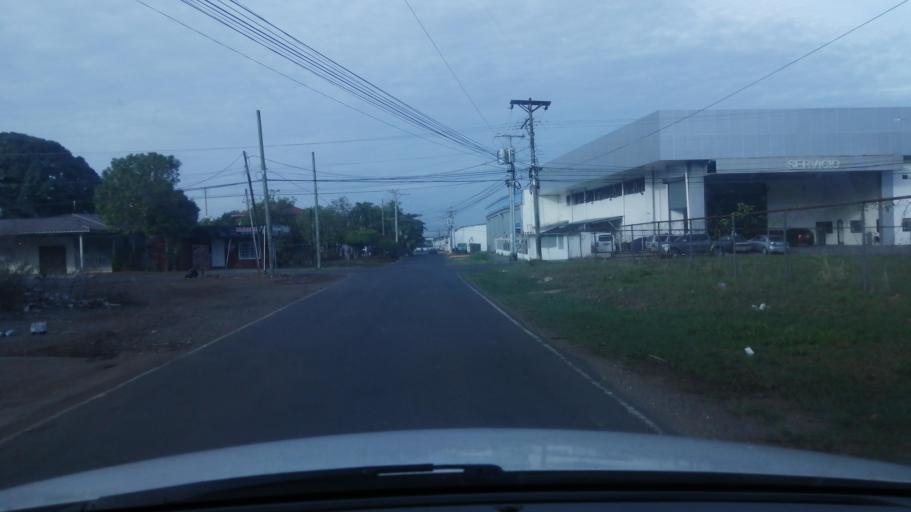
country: PA
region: Chiriqui
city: David
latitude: 8.4349
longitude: -82.4387
